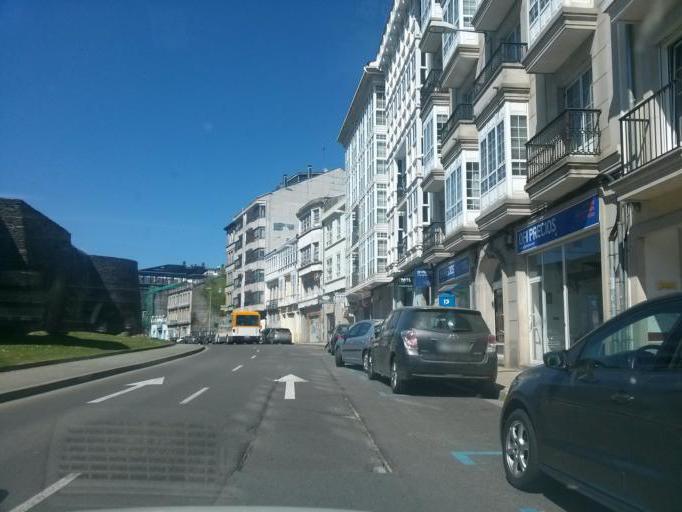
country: ES
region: Galicia
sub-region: Provincia de Lugo
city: Lugo
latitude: 43.0112
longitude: -7.5530
